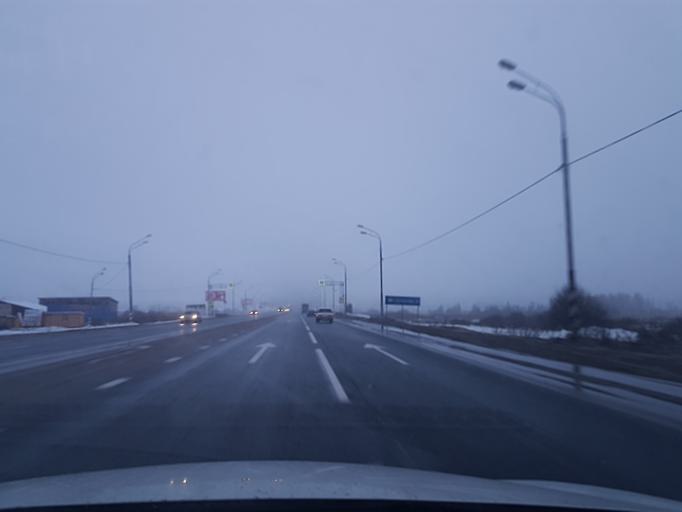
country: RU
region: Moskovskaya
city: Solnechnogorsk
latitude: 56.2277
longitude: 36.9131
